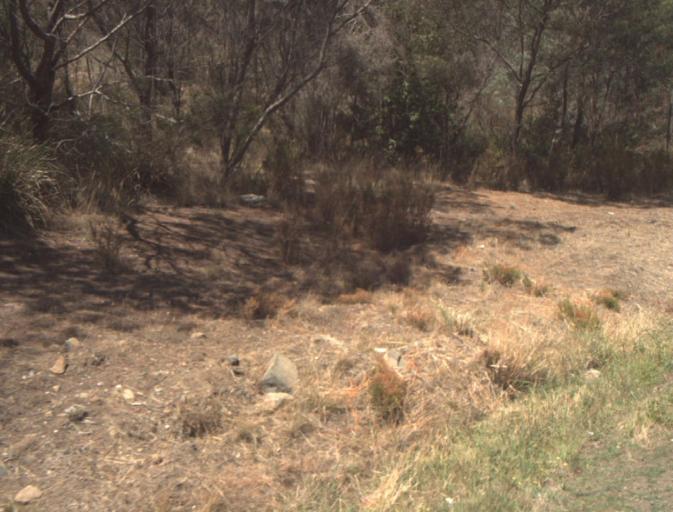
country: AU
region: Tasmania
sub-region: Launceston
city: Mayfield
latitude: -41.3607
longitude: 147.1432
